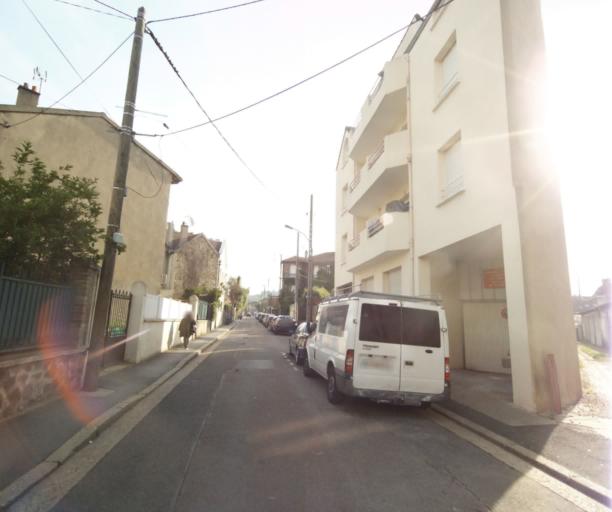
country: FR
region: Ile-de-France
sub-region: Departement du Val-d'Oise
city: Argenteuil
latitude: 48.9501
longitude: 2.2584
